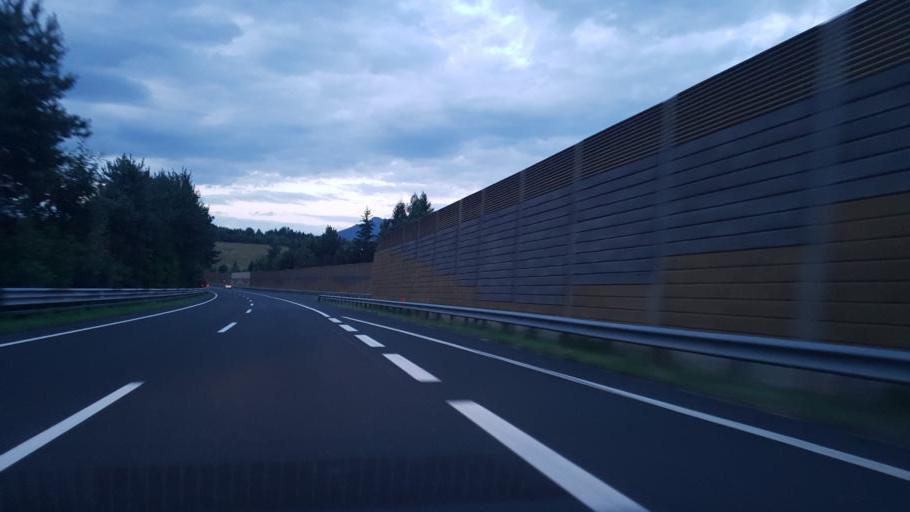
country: AT
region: Carinthia
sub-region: Politischer Bezirk Spittal an der Drau
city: Spittal an der Drau
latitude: 46.8242
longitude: 13.4854
